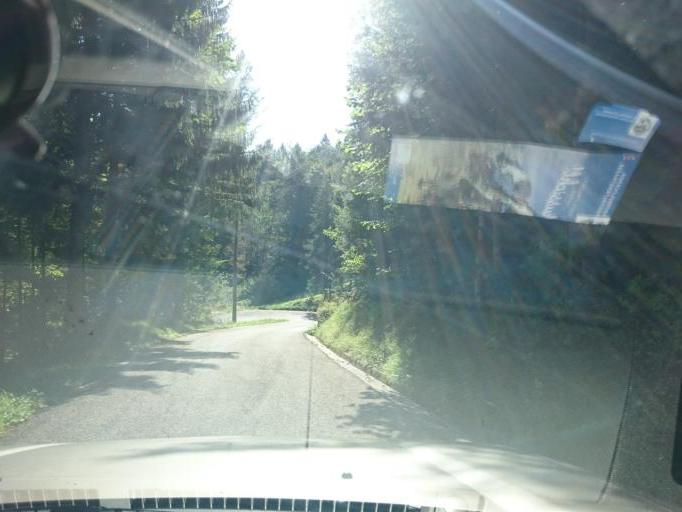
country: IT
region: Friuli Venezia Giulia
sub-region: Provincia di Udine
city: Tarvisio
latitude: 46.4919
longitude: 13.6413
